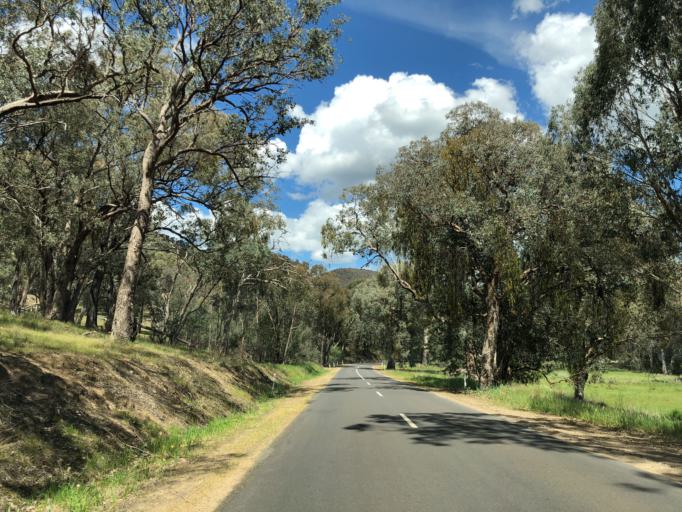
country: AU
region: Victoria
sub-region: Benalla
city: Benalla
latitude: -36.7530
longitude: 146.1191
